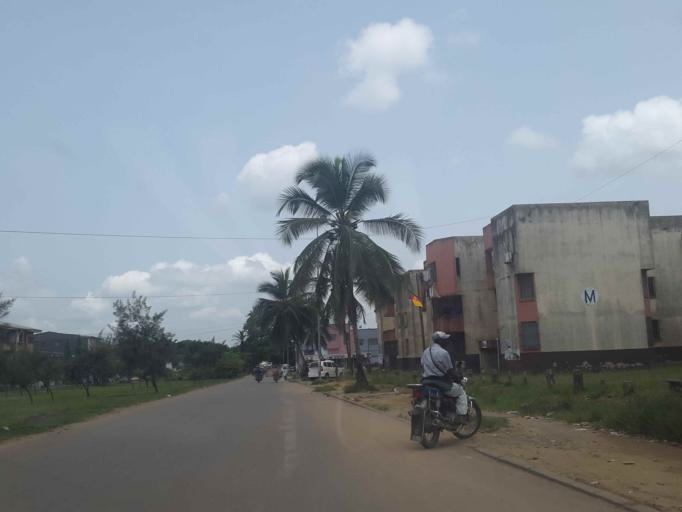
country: CM
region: Littoral
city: Douala
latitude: 4.0926
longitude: 9.7431
